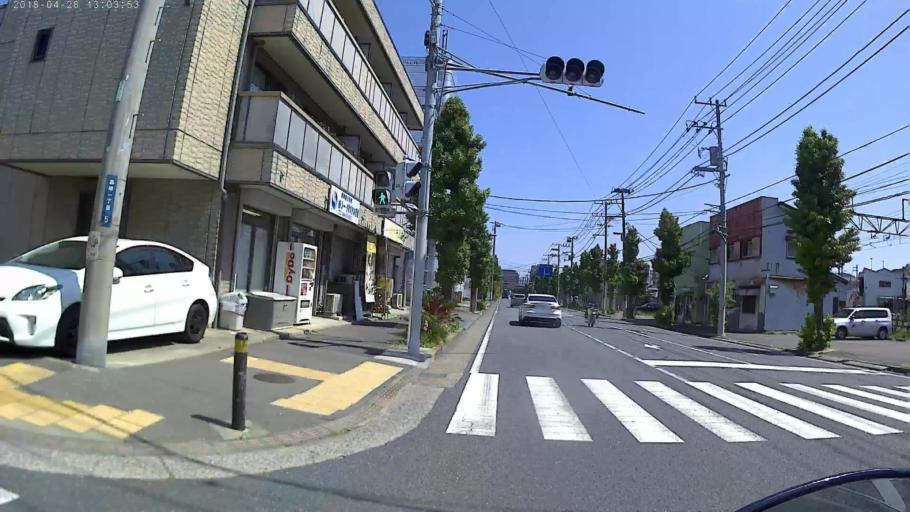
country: JP
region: Kanagawa
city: Yokosuka
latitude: 35.2500
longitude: 139.6803
